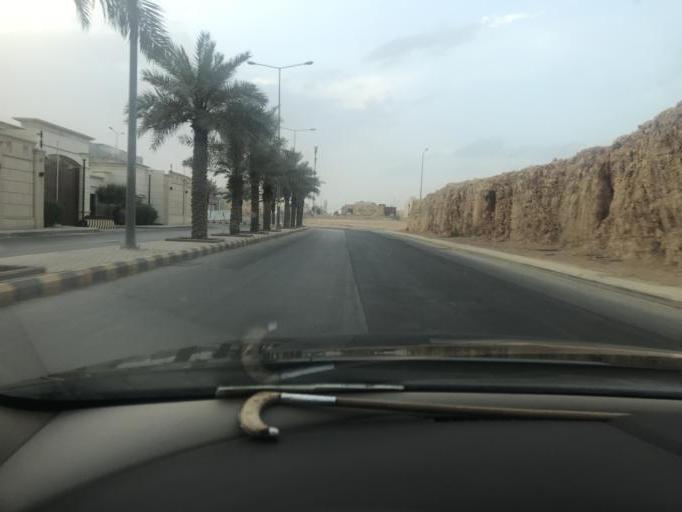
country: SA
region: Ar Riyad
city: Riyadh
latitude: 24.7255
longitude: 46.7490
